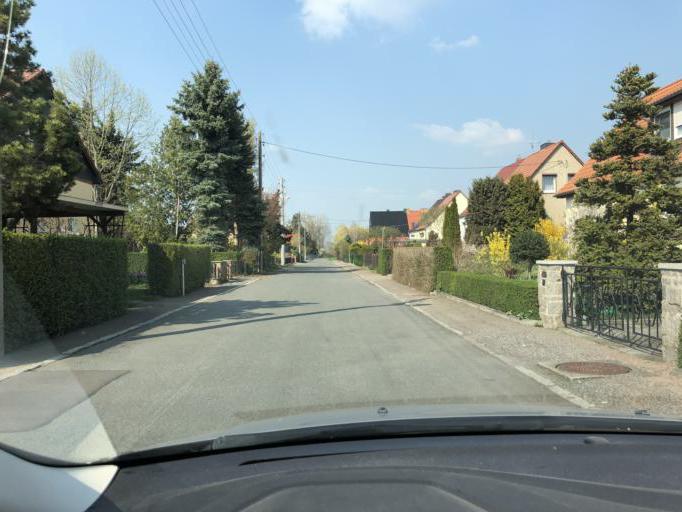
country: DE
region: Saxony-Anhalt
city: Hohenthurm
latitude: 51.5250
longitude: 12.0977
